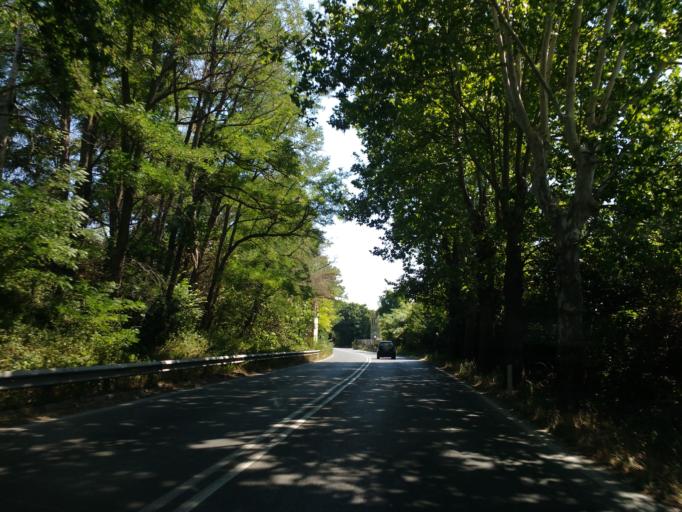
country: IT
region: Latium
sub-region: Citta metropolitana di Roma Capitale
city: Setteville
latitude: 41.9457
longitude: 12.6662
